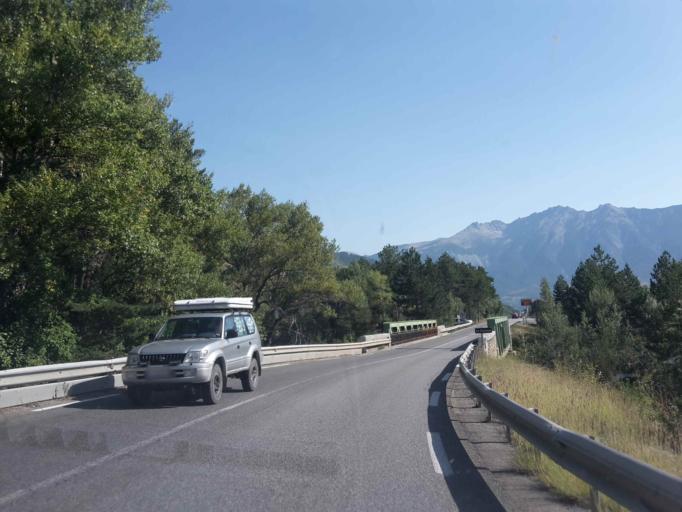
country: FR
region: Provence-Alpes-Cote d'Azur
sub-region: Departement des Hautes-Alpes
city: Guillestre
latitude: 44.6373
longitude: 6.5660
